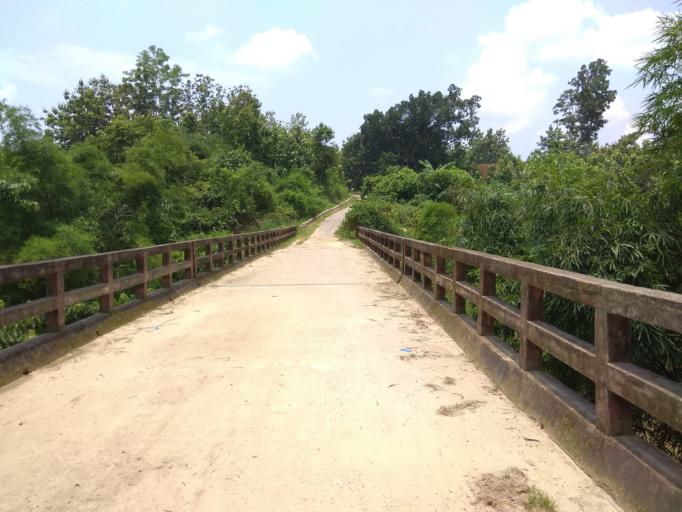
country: BD
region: Chittagong
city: Manikchari
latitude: 22.8864
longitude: 91.9220
